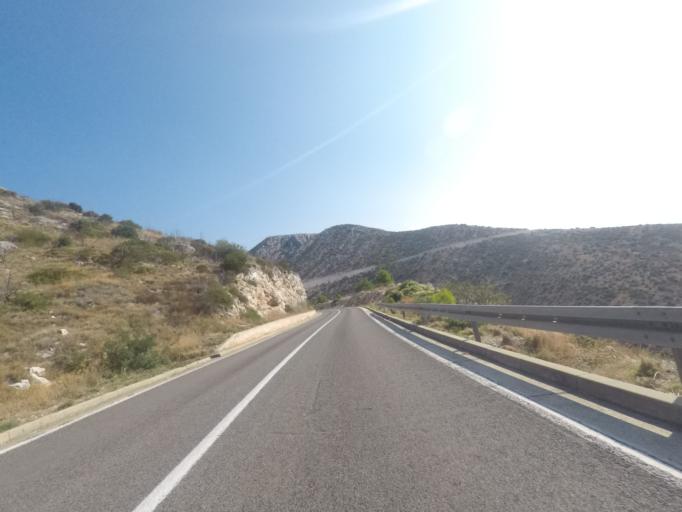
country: HR
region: Splitsko-Dalmatinska
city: Stari Grad
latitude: 43.1479
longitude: 16.5329
